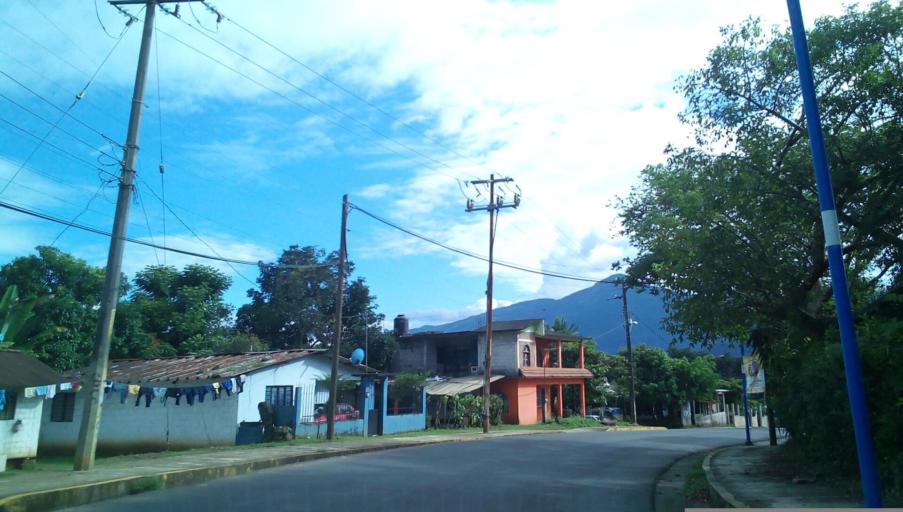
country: MX
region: Veracruz
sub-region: Amatlan de los Reyes
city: Centro de Readaptacion Social
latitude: 18.8241
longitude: -96.9241
